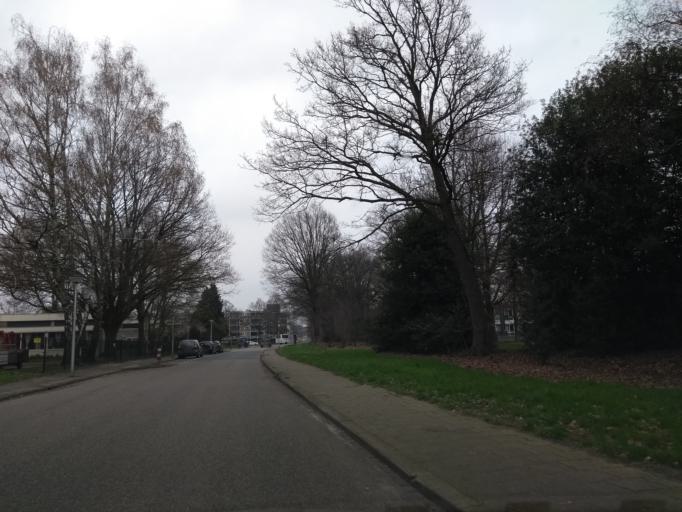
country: NL
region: Overijssel
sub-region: Gemeente Enschede
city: Enschede
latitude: 52.1926
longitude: 6.8750
